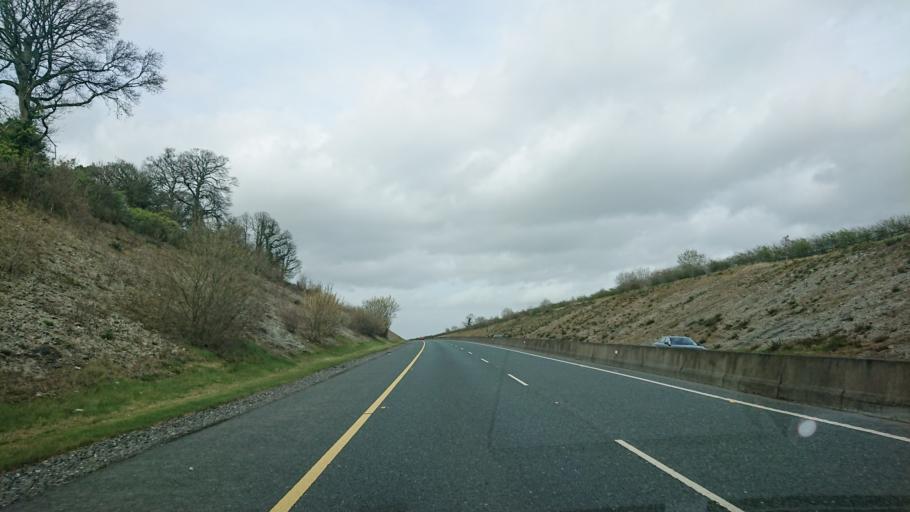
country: IE
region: Leinster
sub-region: Kildare
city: Castledermot
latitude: 52.8586
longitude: -6.8372
